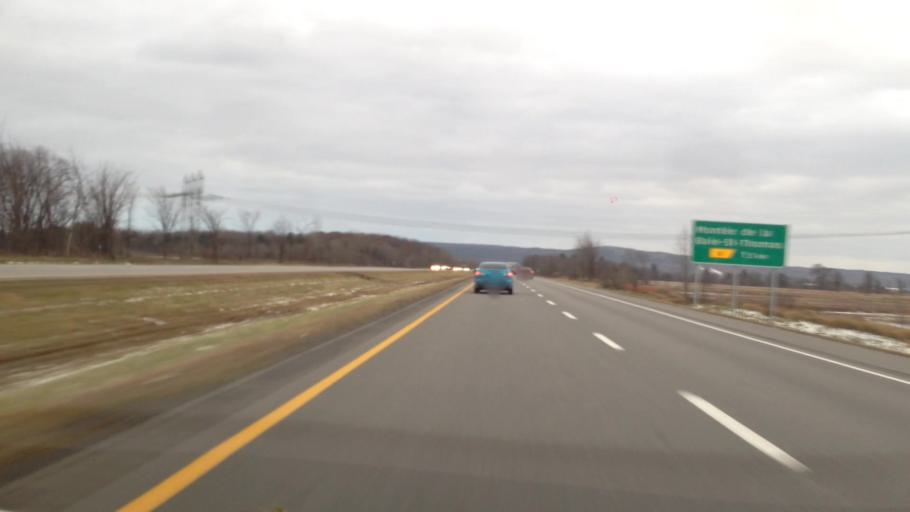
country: CA
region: Quebec
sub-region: Monteregie
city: Rigaud
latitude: 45.5091
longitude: -74.3702
